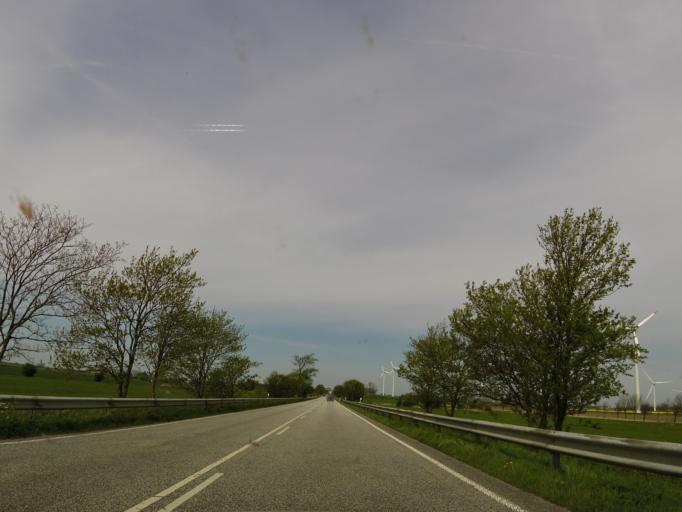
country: DE
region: Schleswig-Holstein
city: Hemme
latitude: 54.2790
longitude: 9.0029
